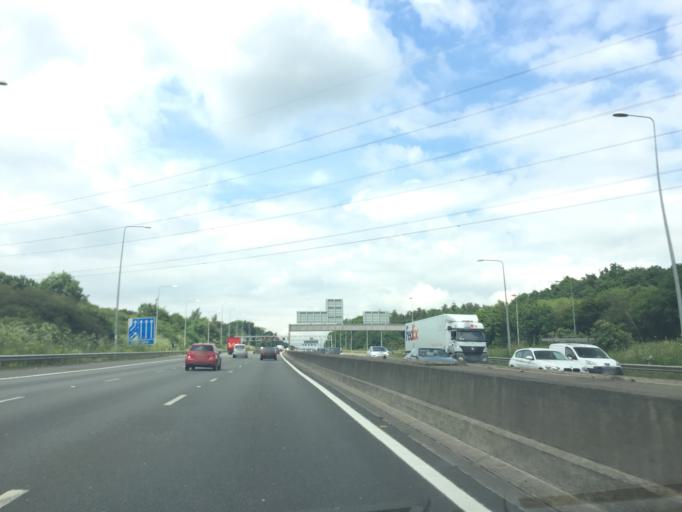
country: GB
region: England
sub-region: Buckinghamshire
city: Gerrards Cross
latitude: 51.5633
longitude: -0.5326
